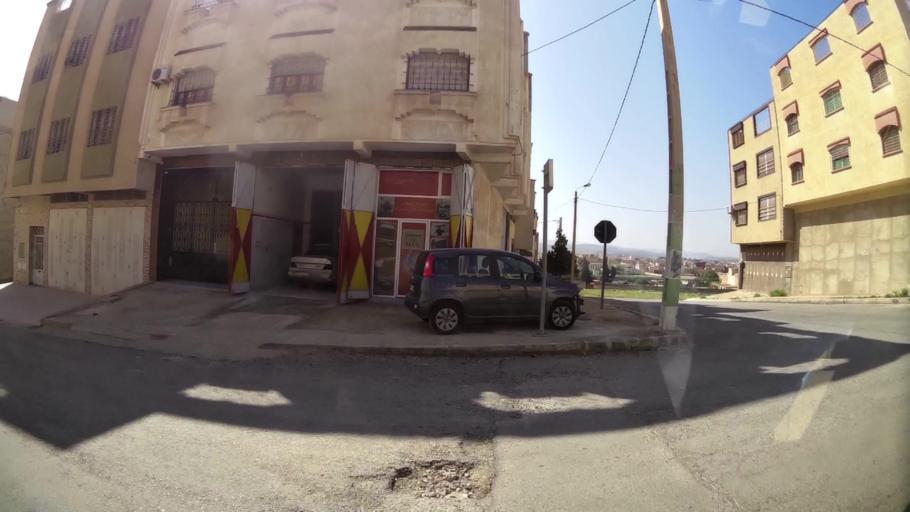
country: MA
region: Oriental
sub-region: Oujda-Angad
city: Oujda
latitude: 34.6752
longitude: -1.9383
